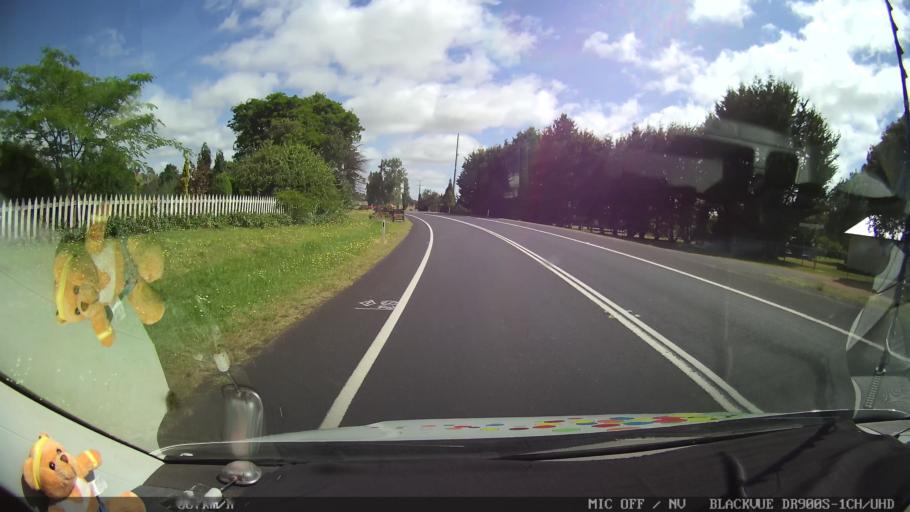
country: AU
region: New South Wales
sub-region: Glen Innes Severn
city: Glen Innes
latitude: -29.9281
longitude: 151.7241
